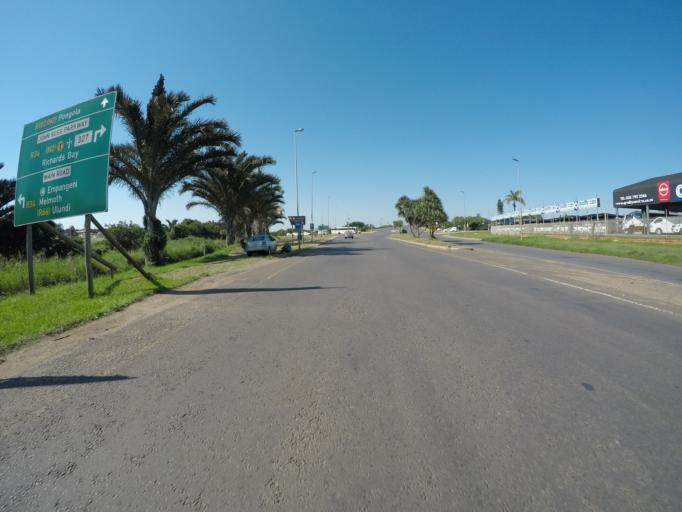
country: ZA
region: KwaZulu-Natal
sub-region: uThungulu District Municipality
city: Empangeni
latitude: -28.7649
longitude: 31.9064
